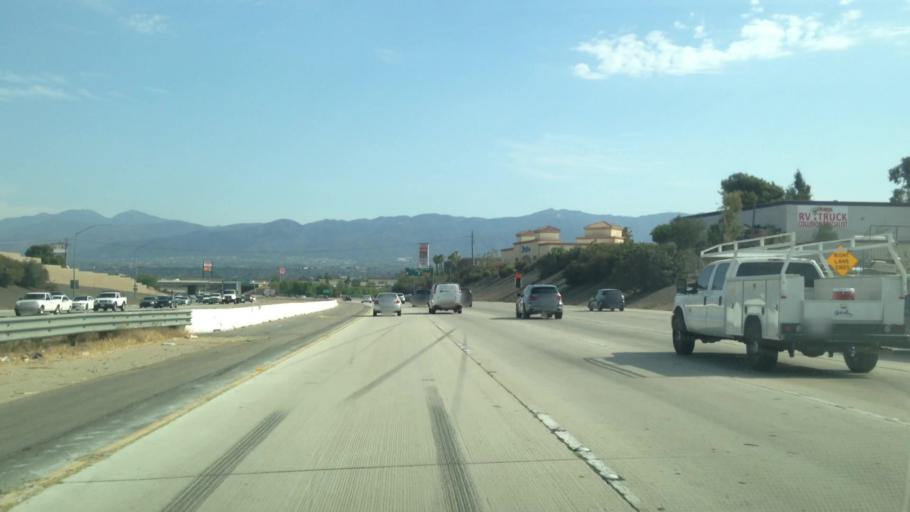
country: US
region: California
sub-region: Riverside County
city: Norco
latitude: 33.9042
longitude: -117.5596
